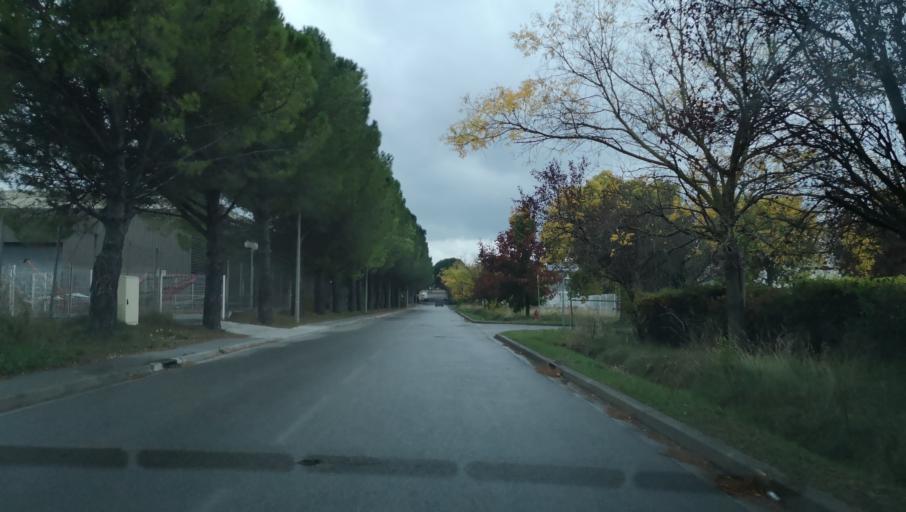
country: FR
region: Provence-Alpes-Cote d'Azur
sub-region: Departement des Bouches-du-Rhone
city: Rousset
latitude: 43.4714
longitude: 5.6088
